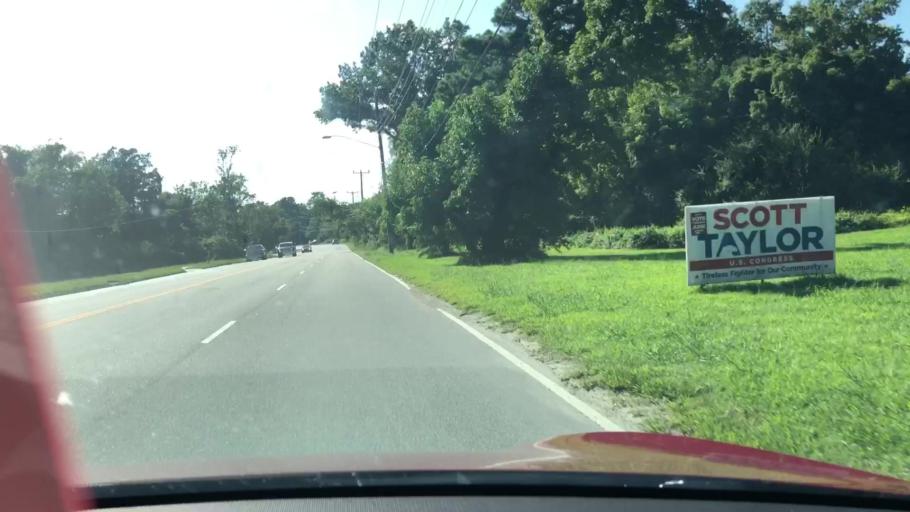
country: US
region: Virginia
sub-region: City of Virginia Beach
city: Virginia Beach
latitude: 36.8422
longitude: -76.0002
